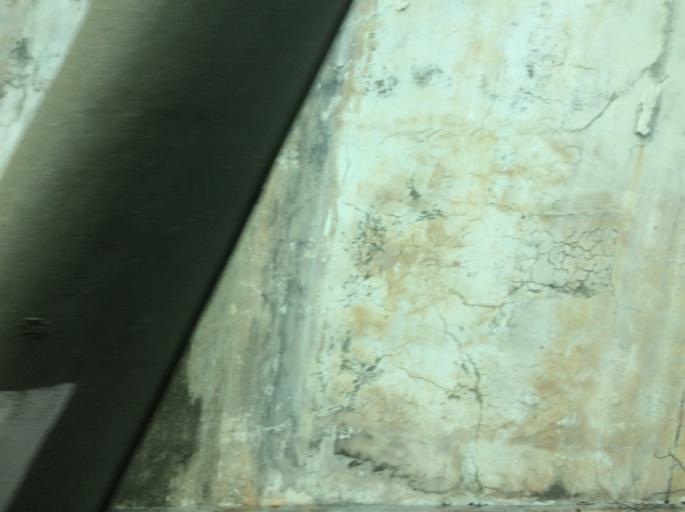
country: TW
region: Taiwan
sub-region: Tainan
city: Tainan
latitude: 22.9941
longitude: 120.2122
